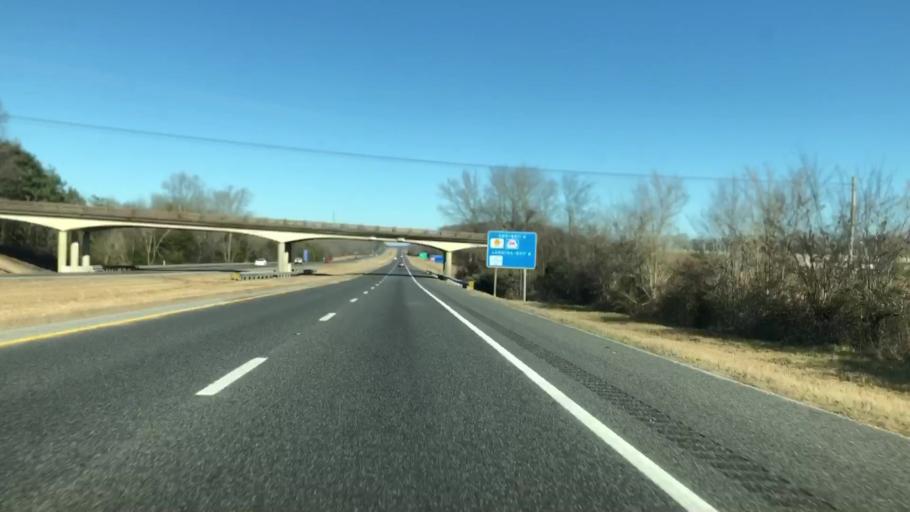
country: US
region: Alabama
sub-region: Limestone County
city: Ardmore
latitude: 35.0614
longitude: -86.8814
